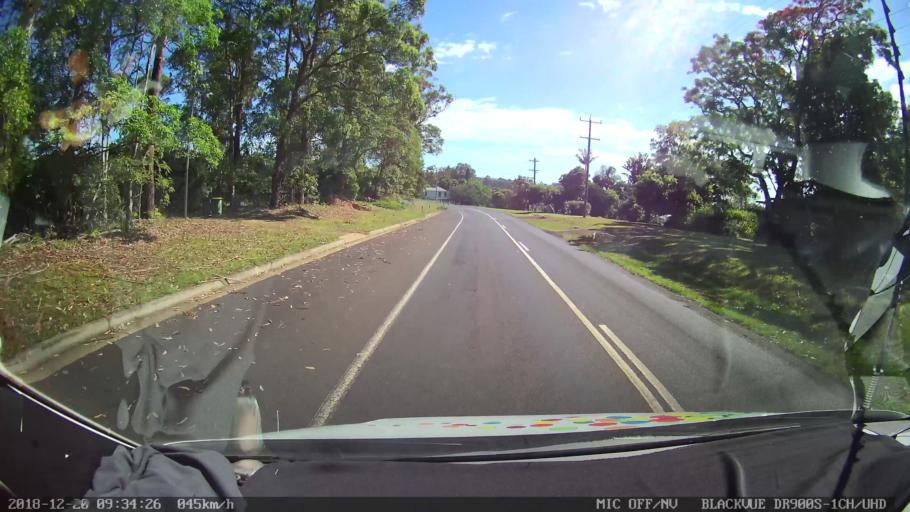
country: AU
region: New South Wales
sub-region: Lismore Municipality
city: Goonellabah
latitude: -28.6903
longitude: 153.3136
